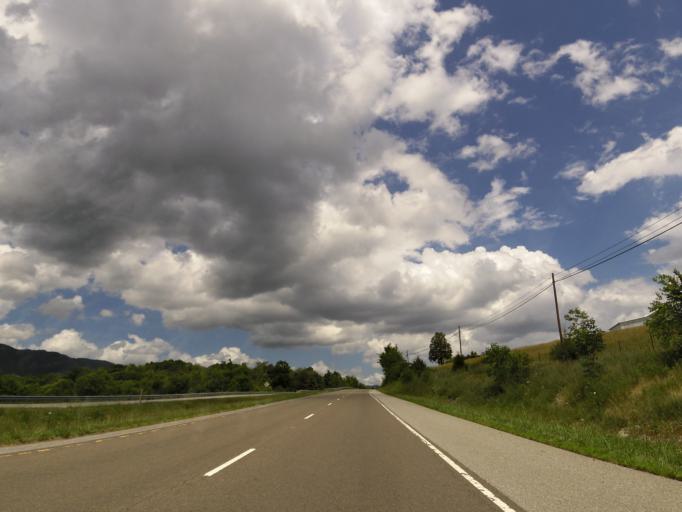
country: US
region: Tennessee
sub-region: Claiborne County
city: Harrogate
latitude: 36.6146
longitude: -83.5652
